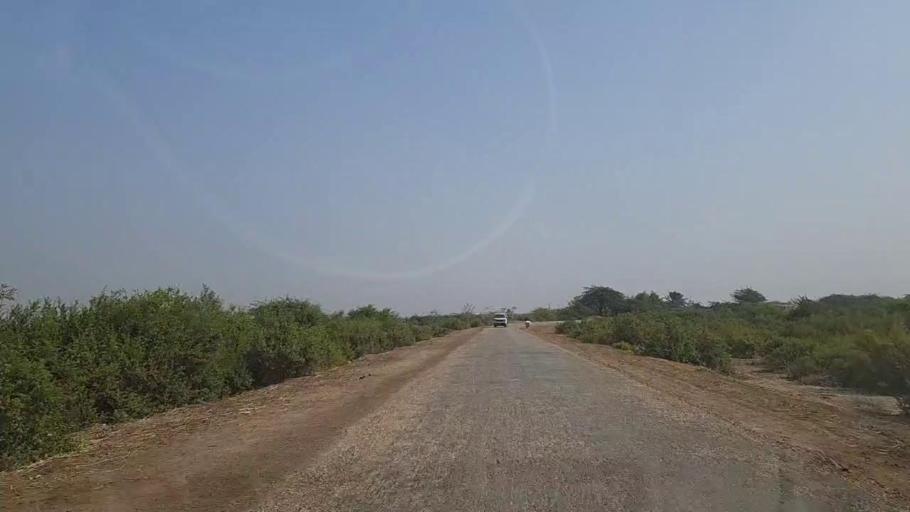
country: PK
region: Sindh
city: Keti Bandar
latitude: 24.2291
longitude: 67.6628
